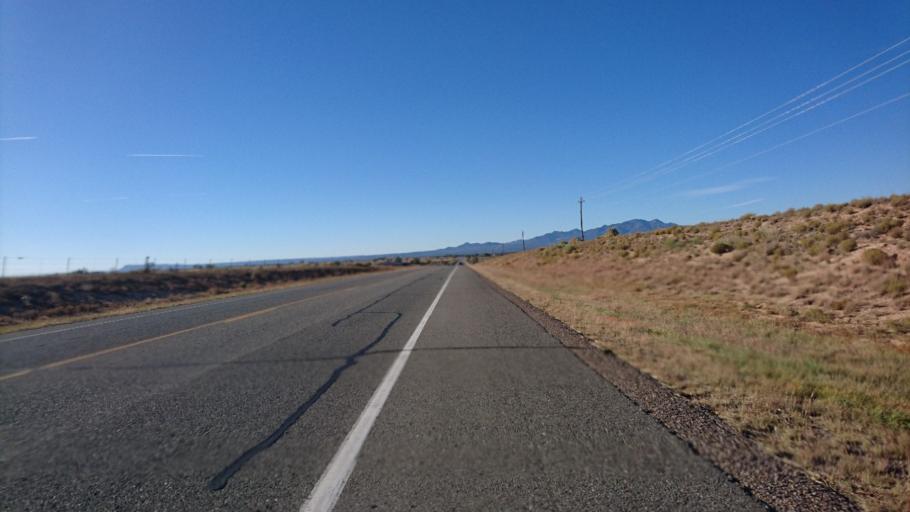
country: US
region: New Mexico
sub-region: Santa Fe County
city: La Cienega
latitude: 35.5063
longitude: -106.0628
